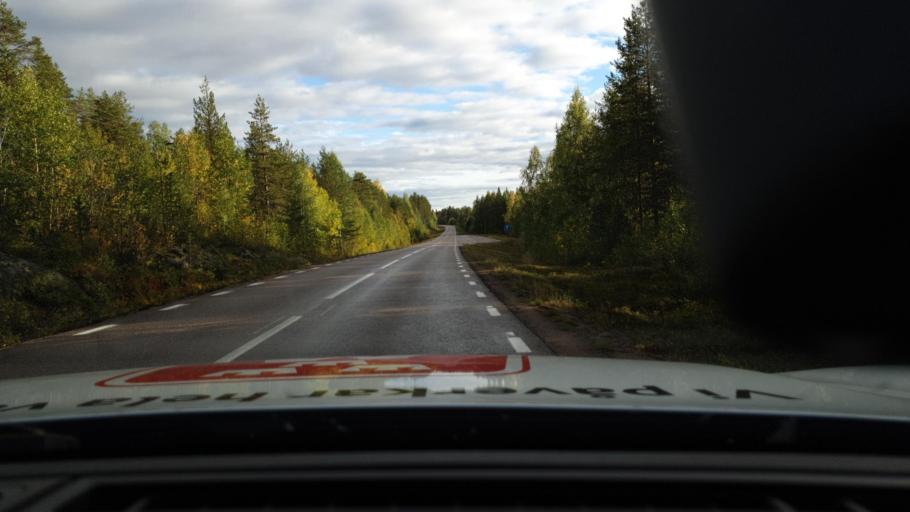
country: SE
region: Norrbotten
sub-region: Overkalix Kommun
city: OEverkalix
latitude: 66.6480
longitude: 22.7204
